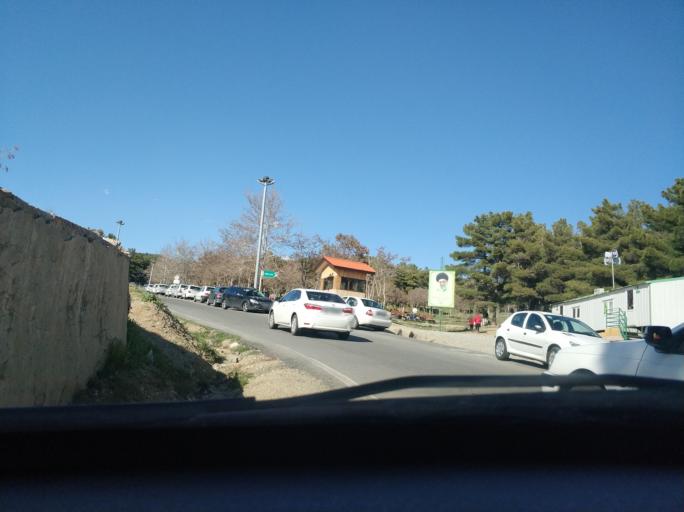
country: IR
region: Tehran
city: Tajrish
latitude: 35.7841
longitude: 51.5580
